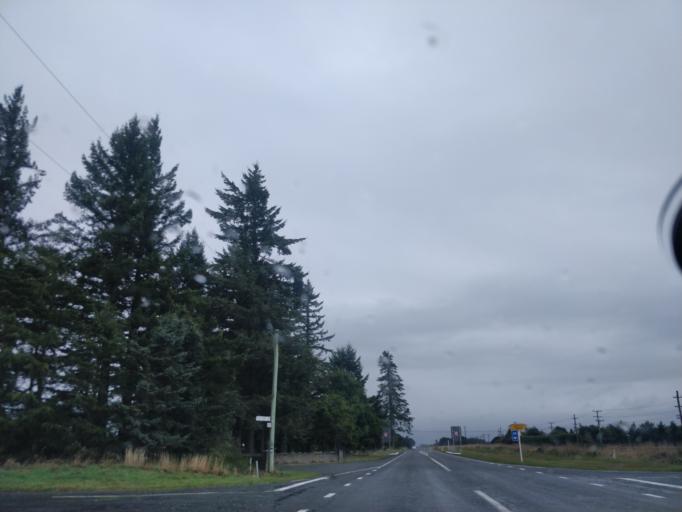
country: NZ
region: Canterbury
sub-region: Selwyn District
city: Darfield
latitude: -43.3861
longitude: 172.0146
